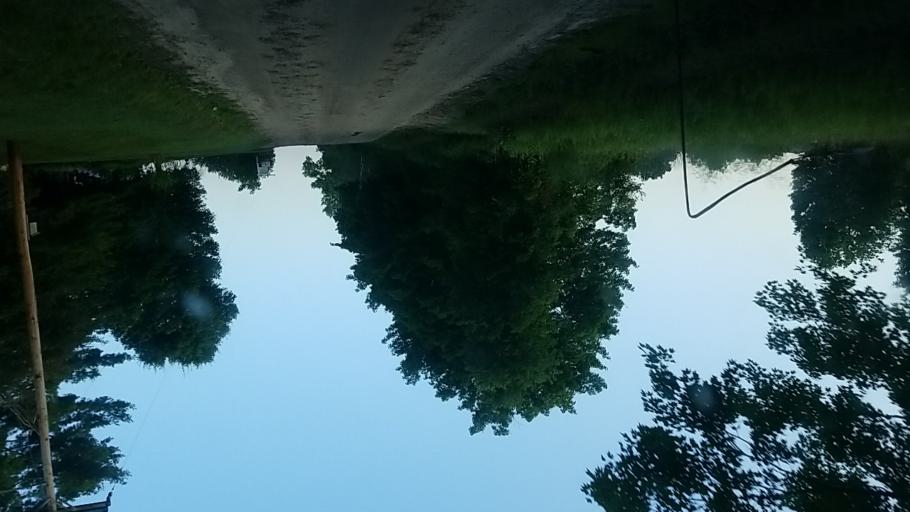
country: US
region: Michigan
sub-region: Osceola County
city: Evart
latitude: 43.9123
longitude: -85.1681
